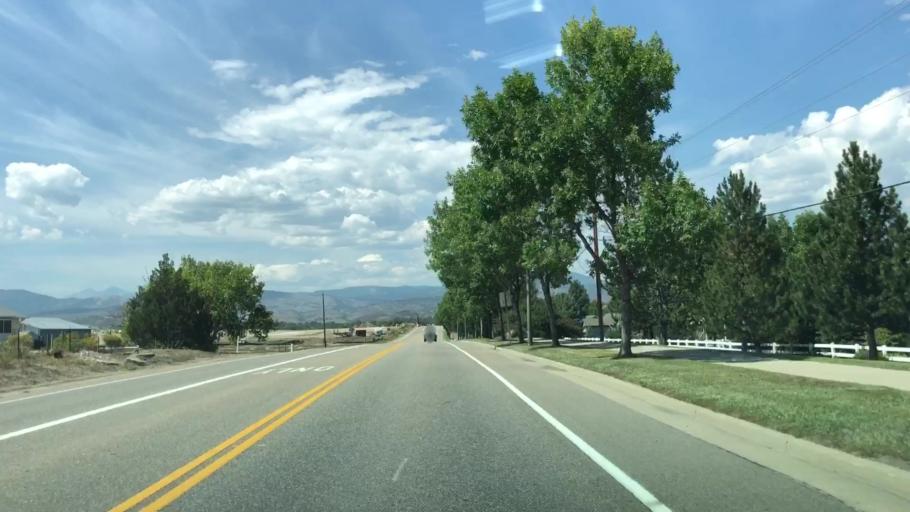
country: US
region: Colorado
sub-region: Larimer County
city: Loveland
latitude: 40.3929
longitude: -105.1320
